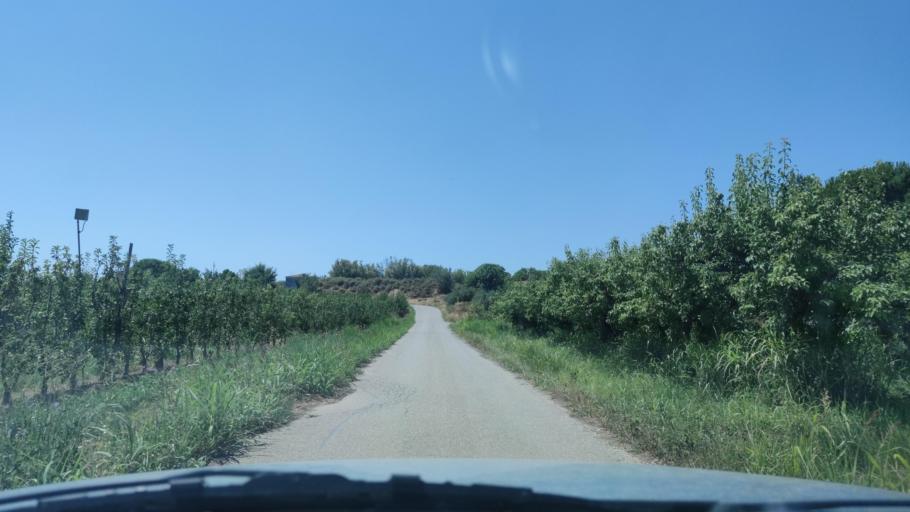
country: ES
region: Catalonia
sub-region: Provincia de Lleida
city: Torrefarrera
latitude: 41.6462
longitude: 0.5901
